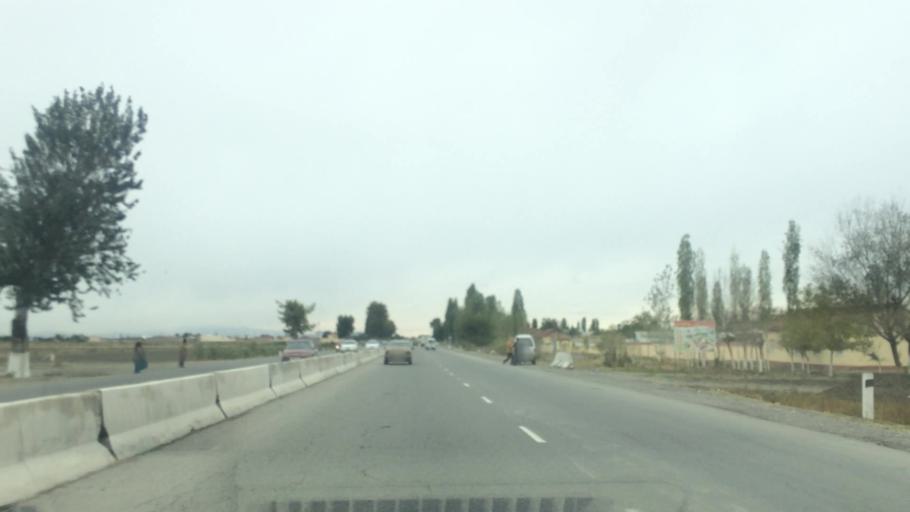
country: UZ
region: Samarqand
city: Jomboy
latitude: 39.7290
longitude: 67.1492
